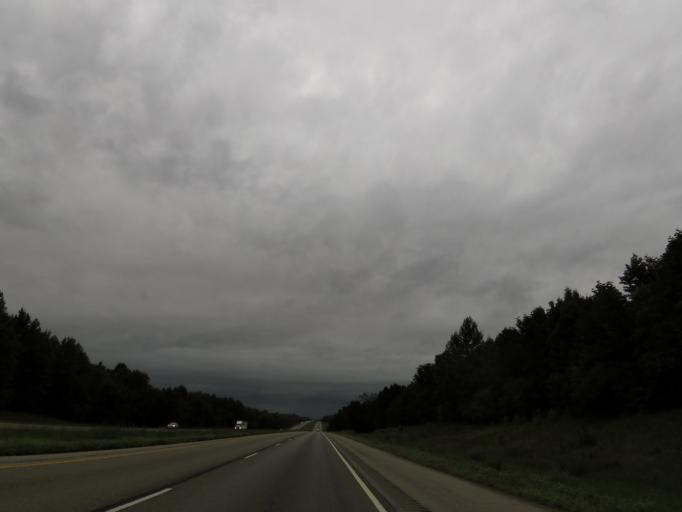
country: US
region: Illinois
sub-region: Massac County
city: Metropolis
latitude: 37.2220
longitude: -88.7035
